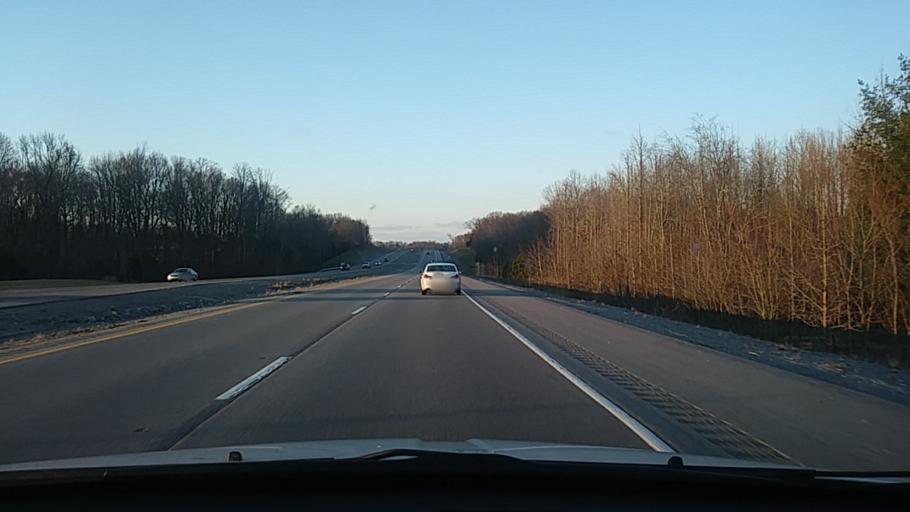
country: US
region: Tennessee
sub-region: Sumner County
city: Portland
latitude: 36.5265
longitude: -86.5104
